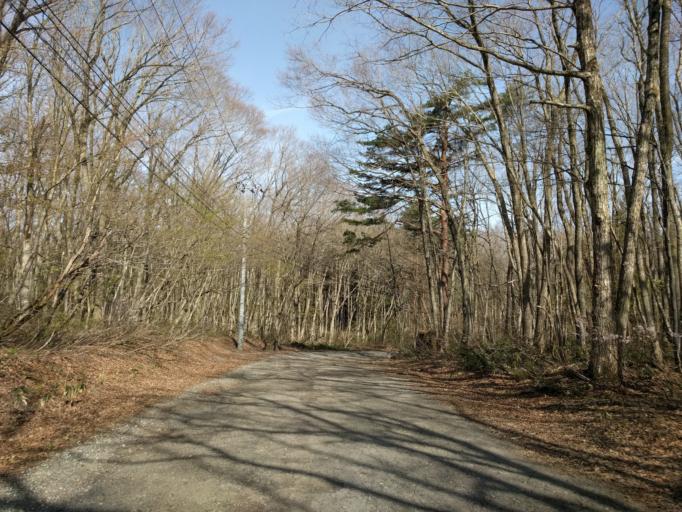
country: JP
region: Fukushima
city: Inawashiro
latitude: 37.5295
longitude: 140.0313
